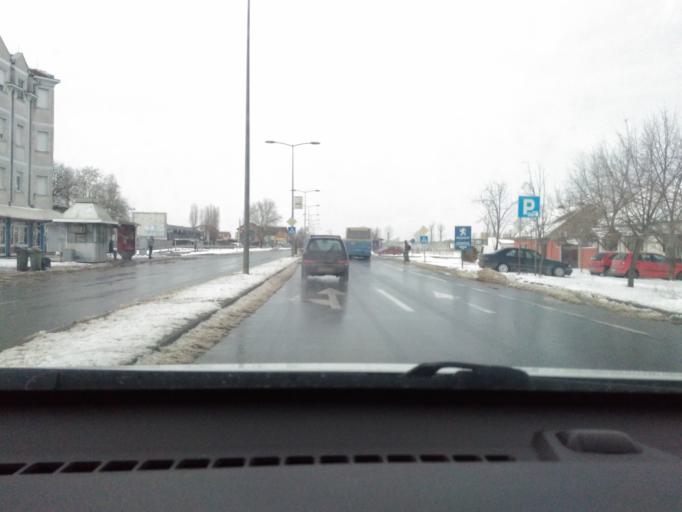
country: RS
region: Autonomna Pokrajina Vojvodina
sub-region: Juznobacki Okrug
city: Novi Sad
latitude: 45.2826
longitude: 19.8351
